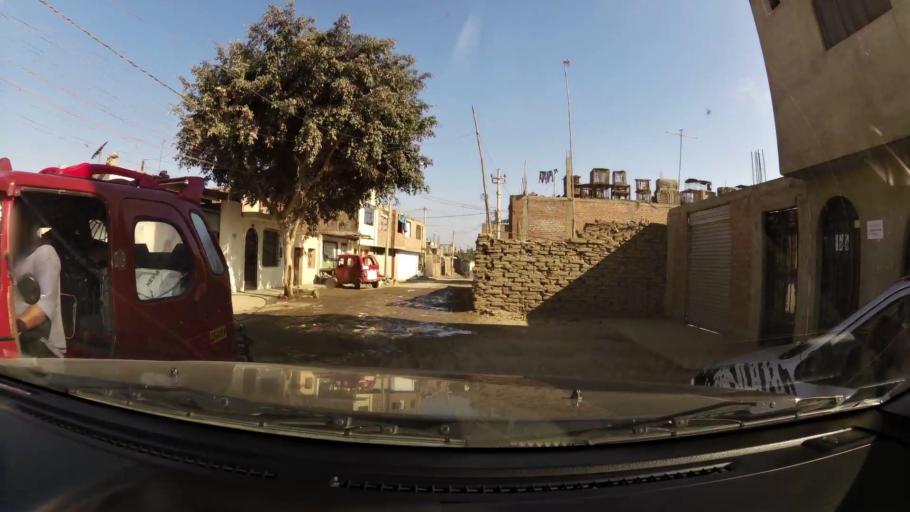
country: PE
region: Ica
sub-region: Provincia de Chincha
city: Chincha Alta
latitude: -13.4136
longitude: -76.1402
